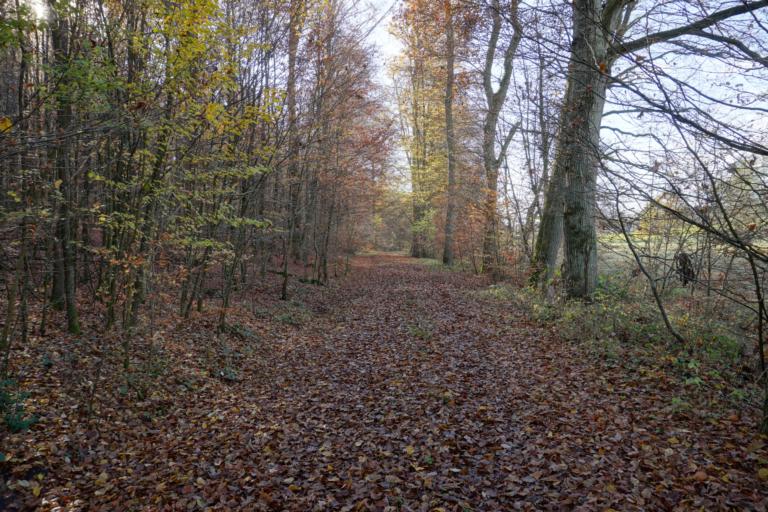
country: DE
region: Baden-Wuerttemberg
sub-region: Karlsruhe Region
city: Aglasterhausen
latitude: 49.3693
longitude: 8.9996
